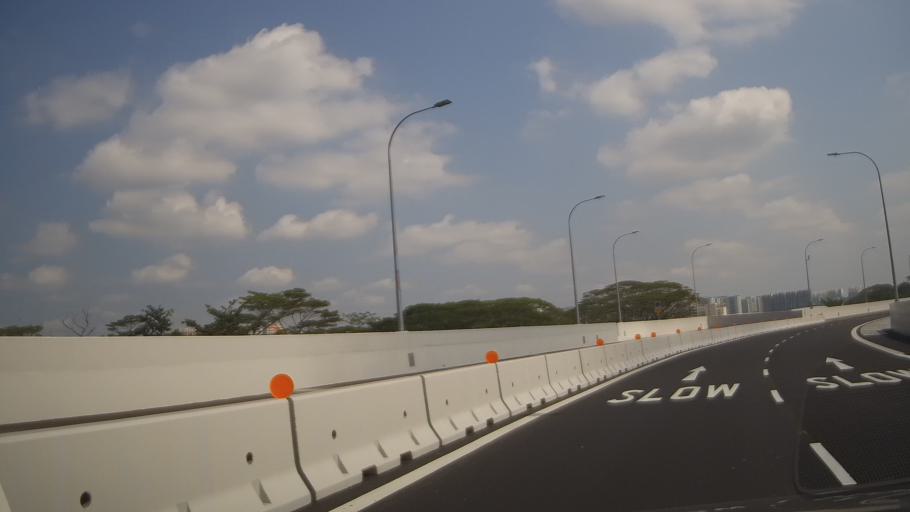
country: MY
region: Johor
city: Kampung Pasir Gudang Baru
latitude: 1.3817
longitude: 103.9146
